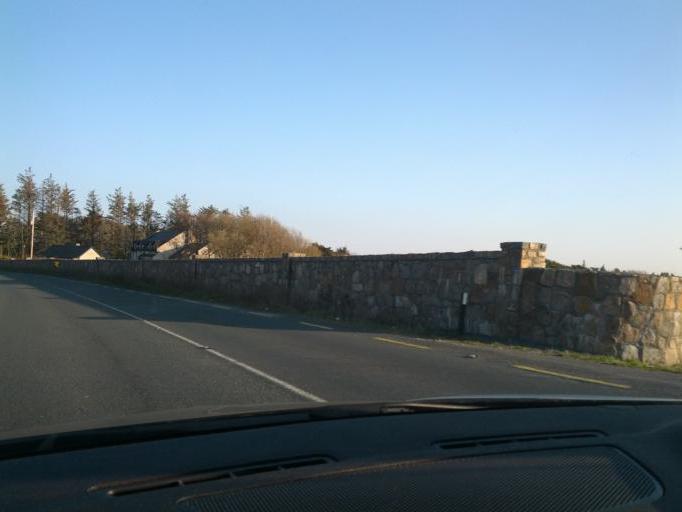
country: IE
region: Connaught
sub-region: County Galway
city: Oughterard
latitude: 53.2812
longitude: -9.5387
